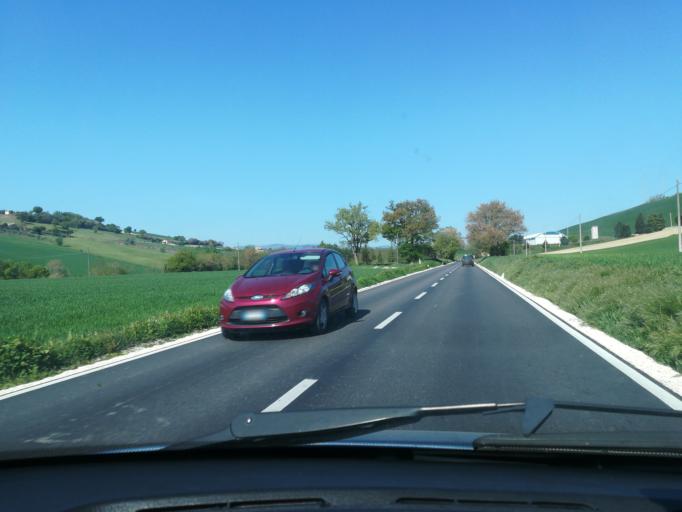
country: IT
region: The Marches
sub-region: Provincia di Macerata
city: Villa Potenza
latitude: 43.3276
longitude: 13.3971
